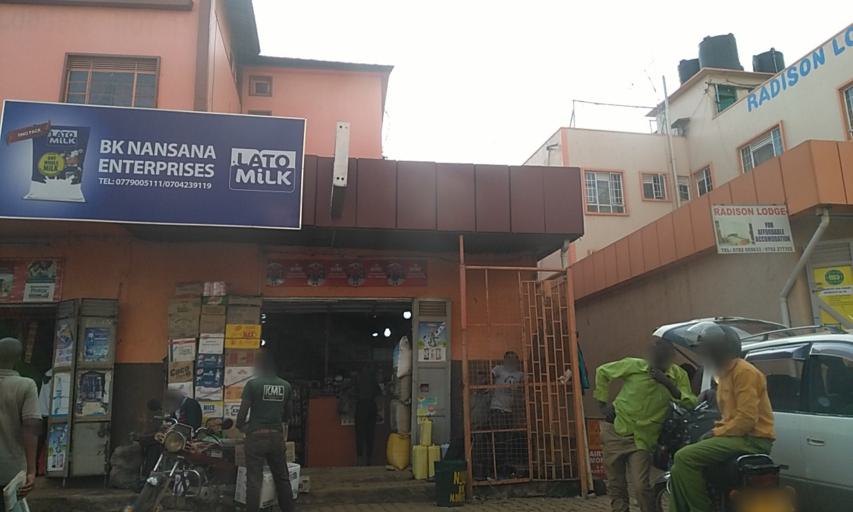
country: UG
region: Central Region
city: Kampala Central Division
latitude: 0.3156
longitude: 32.5724
